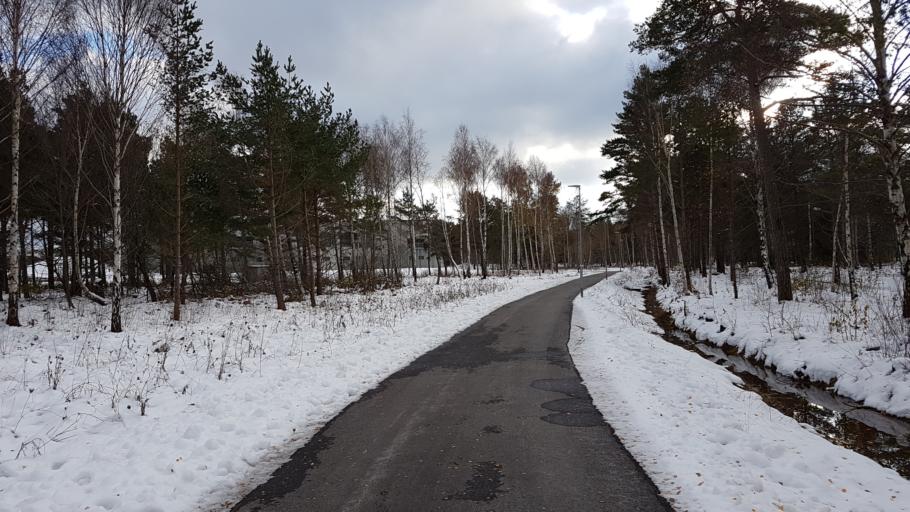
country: SE
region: Gotland
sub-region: Gotland
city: Vibble
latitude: 57.6081
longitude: 18.2805
